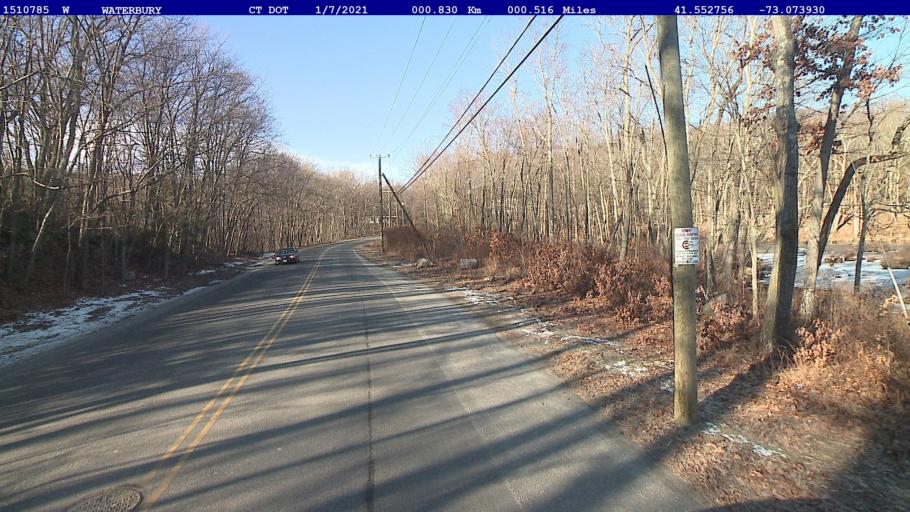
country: US
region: Connecticut
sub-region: New Haven County
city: Waterbury
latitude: 41.5528
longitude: -73.0739
